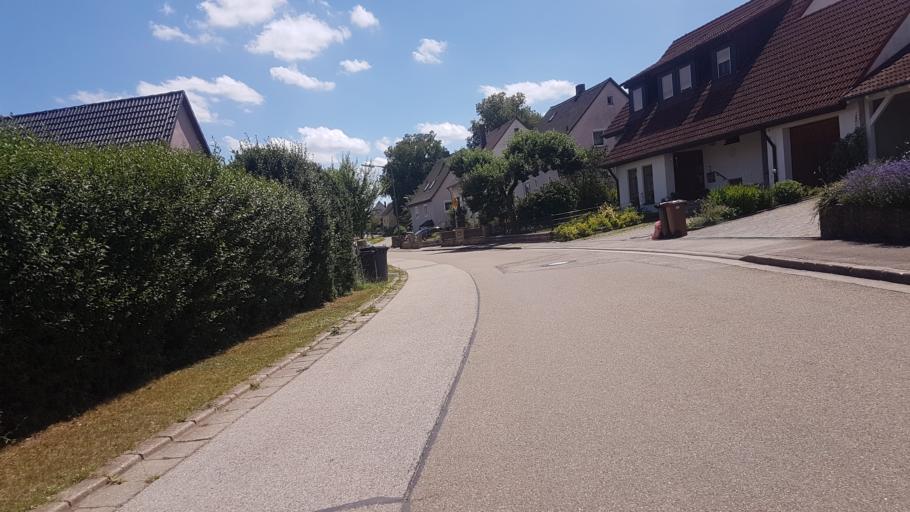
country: DE
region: Bavaria
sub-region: Regierungsbezirk Mittelfranken
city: Leutershausen
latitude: 49.3114
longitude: 10.3887
